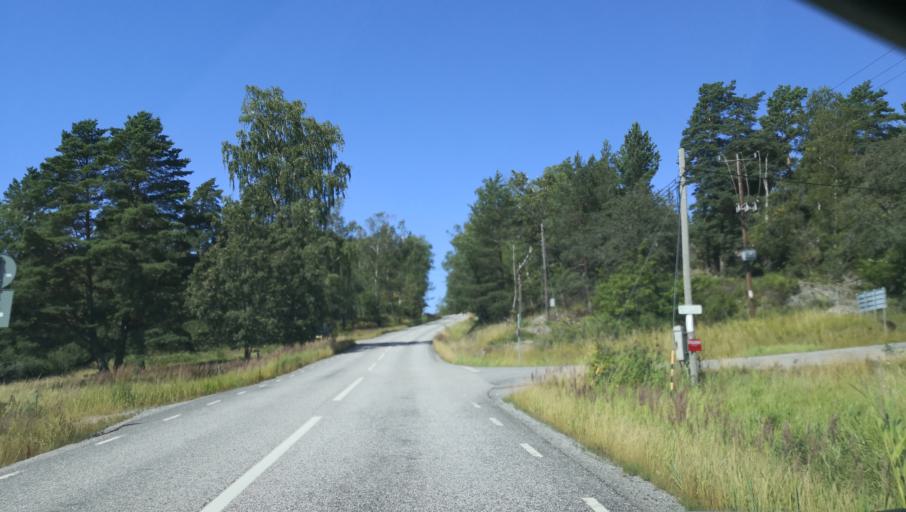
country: SE
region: Stockholm
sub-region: Varmdo Kommun
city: Mortnas
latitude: 59.3941
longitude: 18.4664
